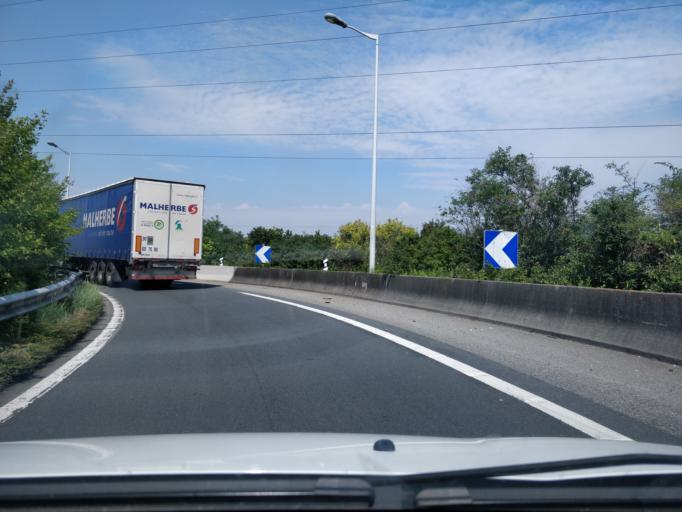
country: FR
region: Haute-Normandie
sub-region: Departement de la Seine-Maritime
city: Harfleur
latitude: 49.4993
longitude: 0.2128
